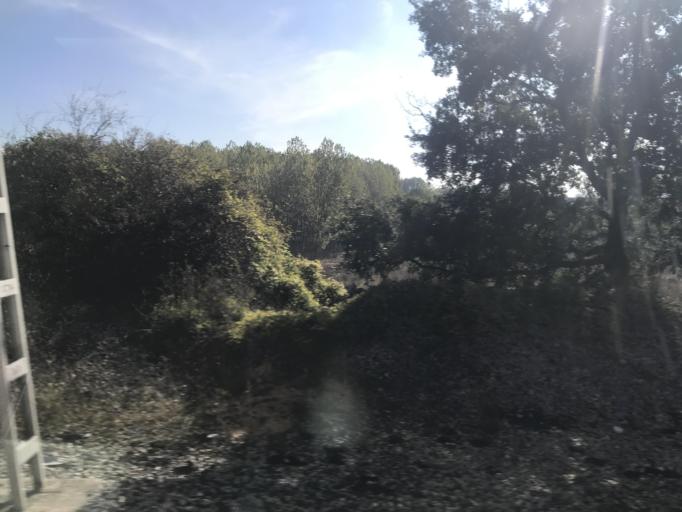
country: ES
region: Basque Country
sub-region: Provincia de Alava
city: Arminon
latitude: 42.7751
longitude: -2.8298
